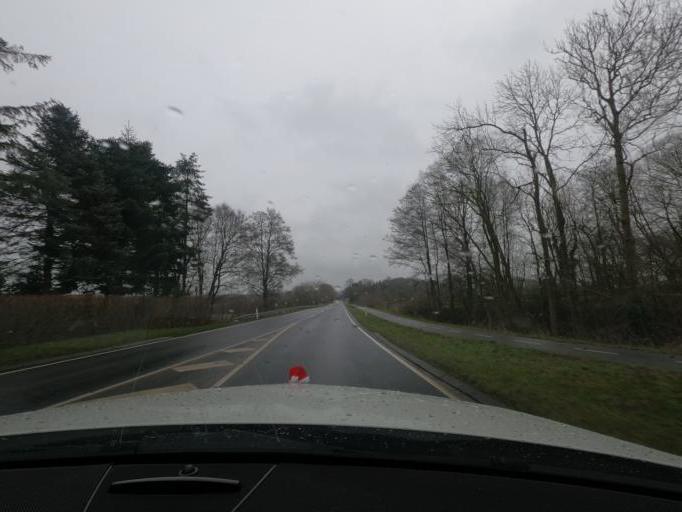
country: DK
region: South Denmark
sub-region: Haderslev Kommune
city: Starup
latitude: 55.2436
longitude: 9.5497
